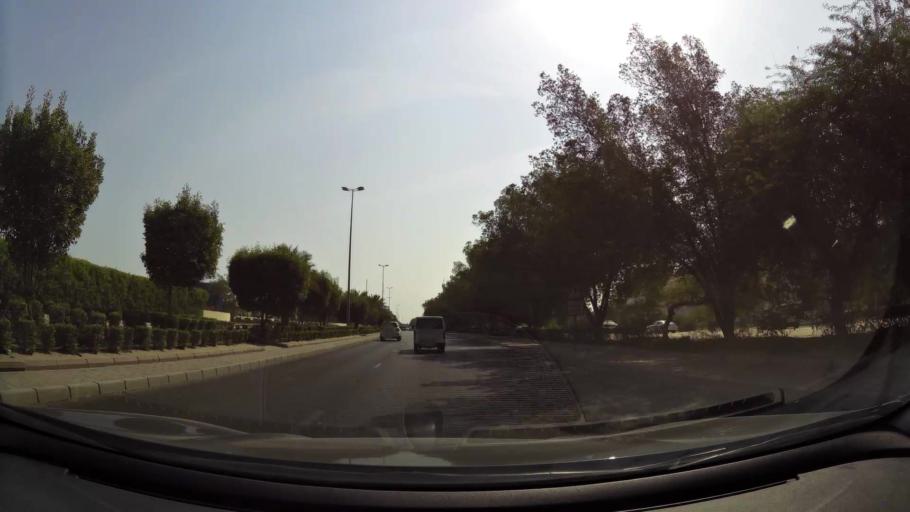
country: KW
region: Al Ahmadi
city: Al Manqaf
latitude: 29.1167
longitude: 48.1342
